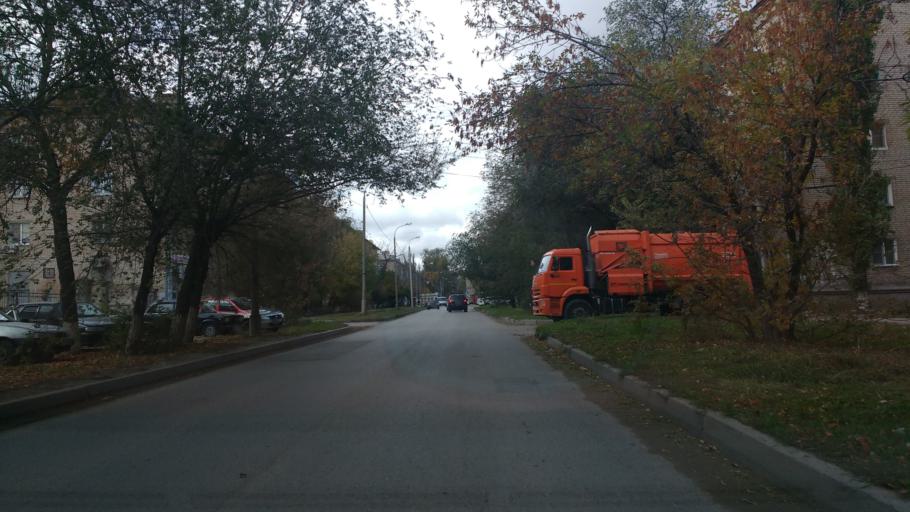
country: RU
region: Volgograd
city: Vodstroy
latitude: 48.7741
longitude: 44.5474
